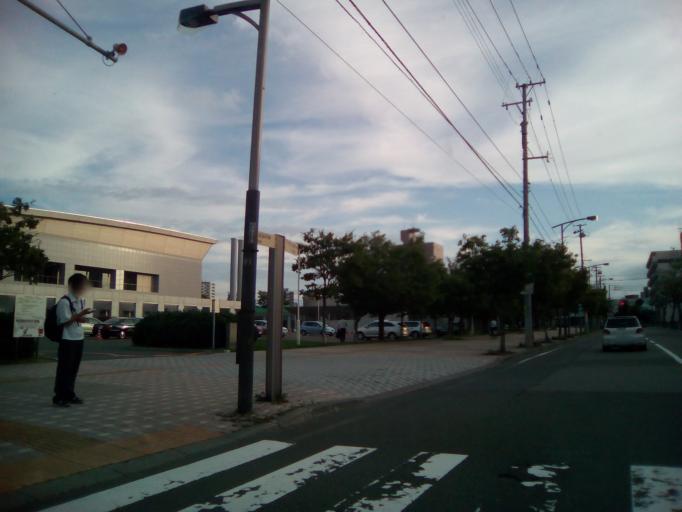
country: JP
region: Hokkaido
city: Sapporo
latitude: 43.0444
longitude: 141.3755
